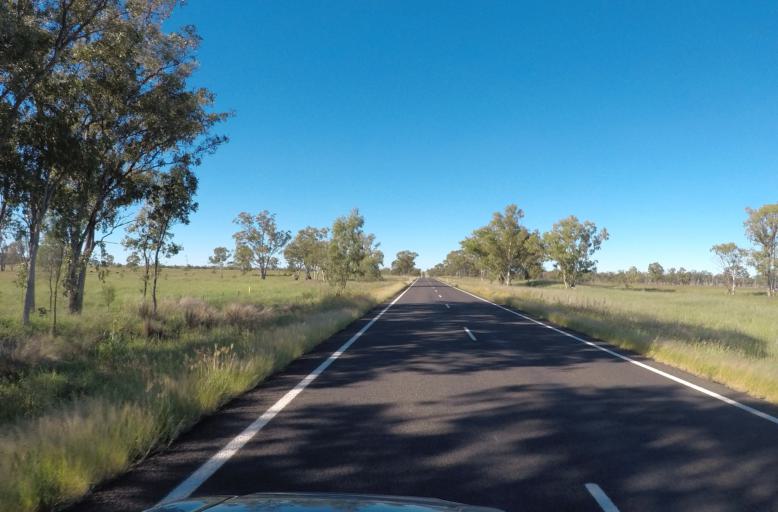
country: AU
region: Queensland
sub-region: Maranoa
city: Roma
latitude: -26.1321
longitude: 148.6548
